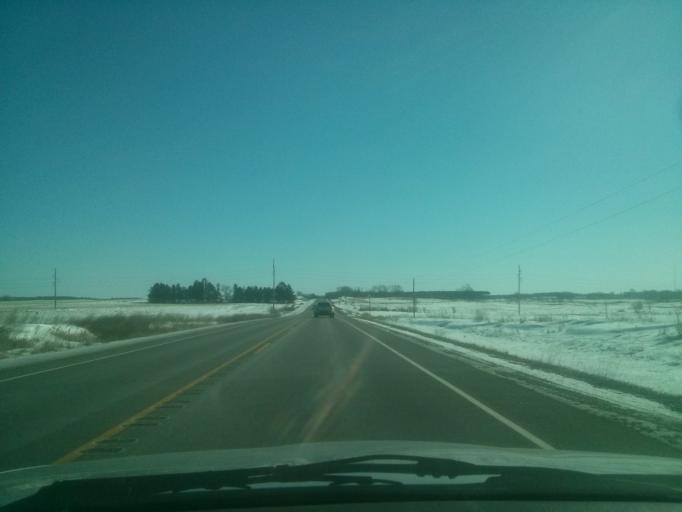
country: US
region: Wisconsin
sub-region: Polk County
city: Clear Lake
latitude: 45.1363
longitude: -92.3052
